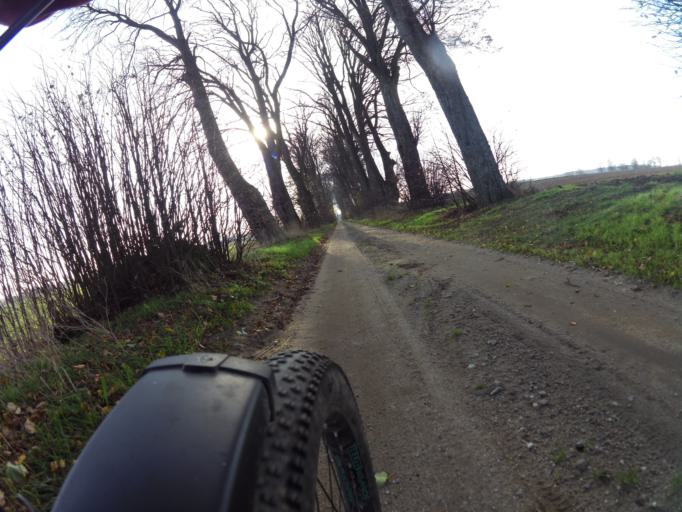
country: PL
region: Pomeranian Voivodeship
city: Strzelno
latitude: 54.7527
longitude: 18.2905
